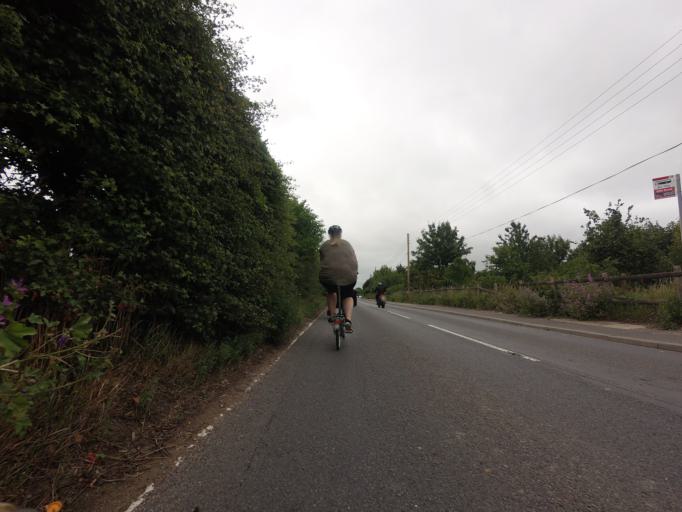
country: GB
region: England
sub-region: Kent
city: Longfield
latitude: 51.4082
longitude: 0.2823
